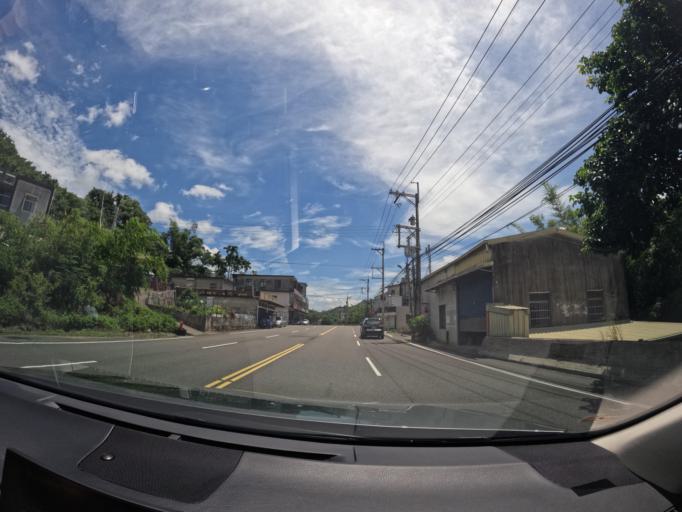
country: TW
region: Taiwan
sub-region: Miaoli
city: Miaoli
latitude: 24.5242
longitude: 120.9129
